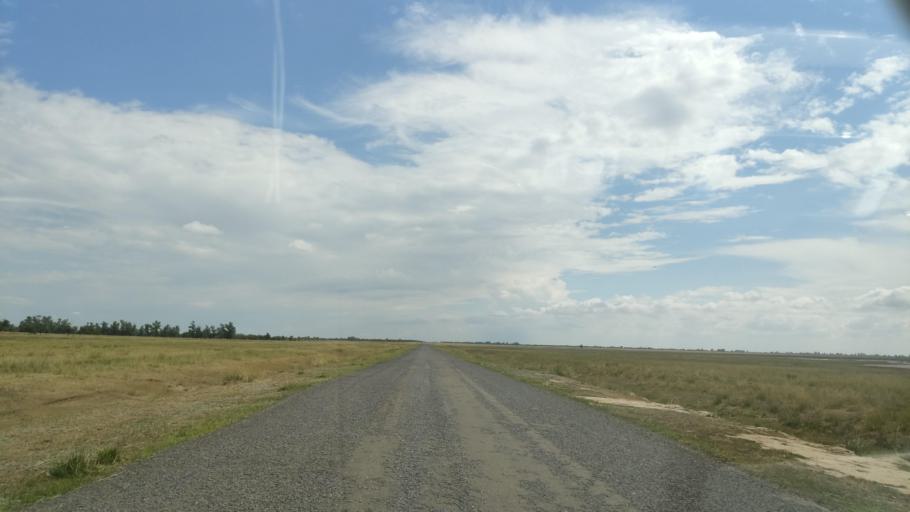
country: KZ
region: Pavlodar
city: Pavlodar
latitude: 52.6355
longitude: 76.9294
